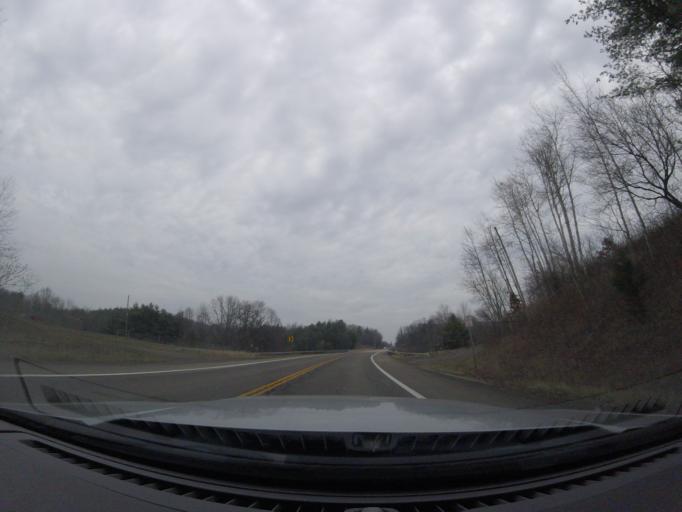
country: US
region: New York
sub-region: Yates County
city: Dundee
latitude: 42.4793
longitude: -76.9244
